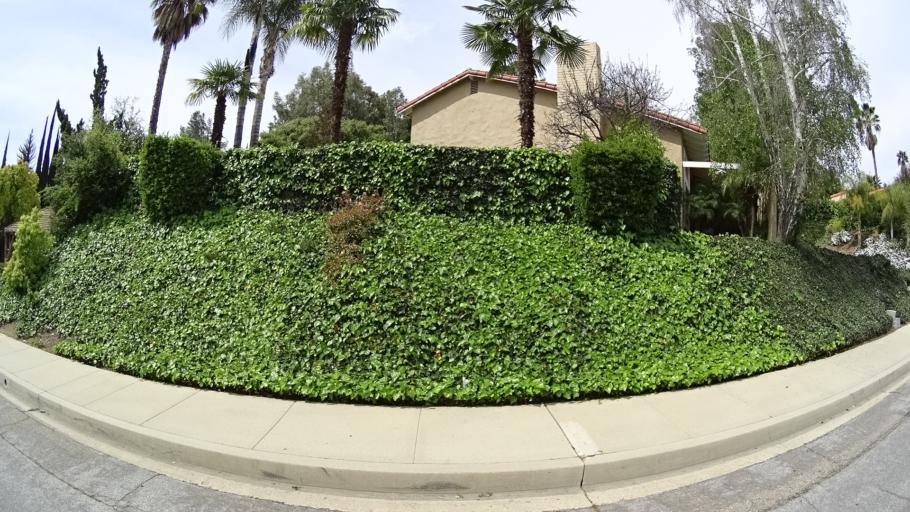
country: US
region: California
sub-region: Ventura County
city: Thousand Oaks
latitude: 34.1429
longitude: -118.8355
